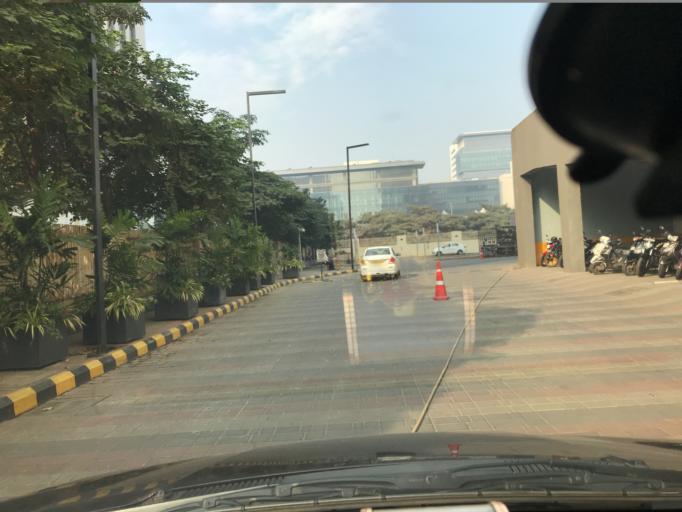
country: IN
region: Maharashtra
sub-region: Thane
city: Airoli
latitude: 19.1753
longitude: 72.9924
